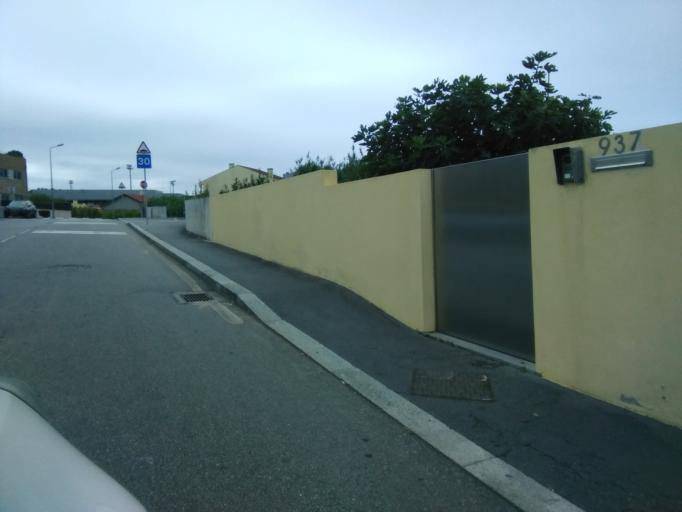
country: PT
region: Porto
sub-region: Matosinhos
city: Lavra
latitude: 41.2560
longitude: -8.7223
